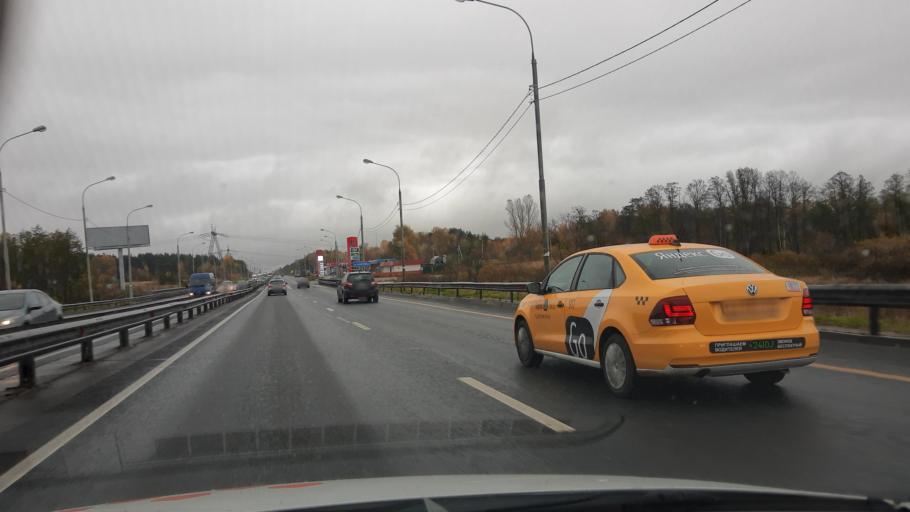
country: RU
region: Moskovskaya
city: Obukhovo
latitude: 55.8300
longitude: 38.2857
